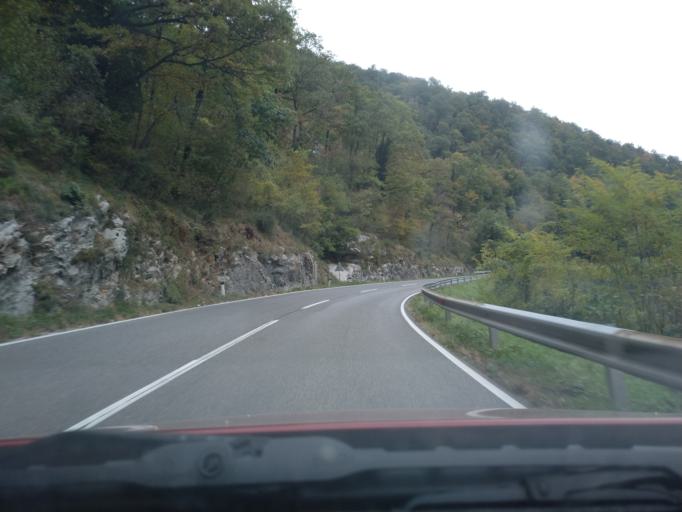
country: SI
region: Kanal
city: Deskle
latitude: 46.0155
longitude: 13.6103
